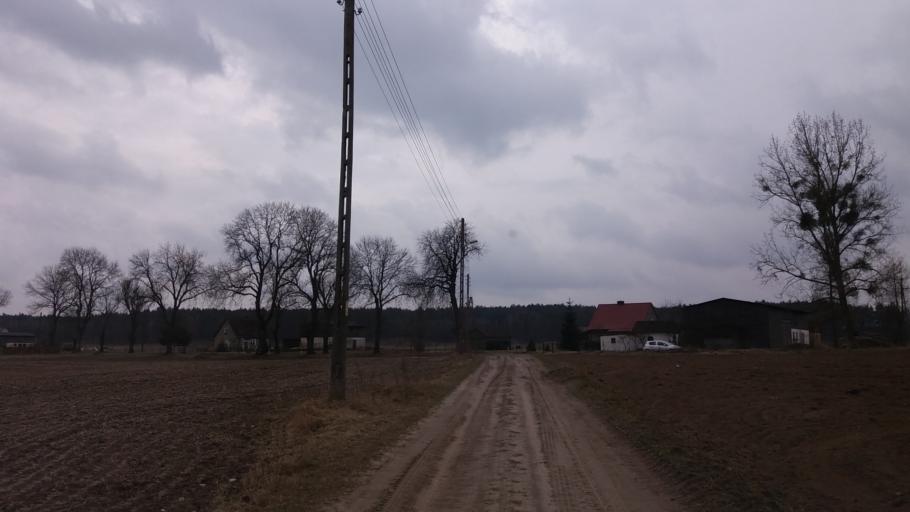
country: PL
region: West Pomeranian Voivodeship
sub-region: Powiat choszczenski
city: Bierzwnik
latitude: 53.1426
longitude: 15.6801
